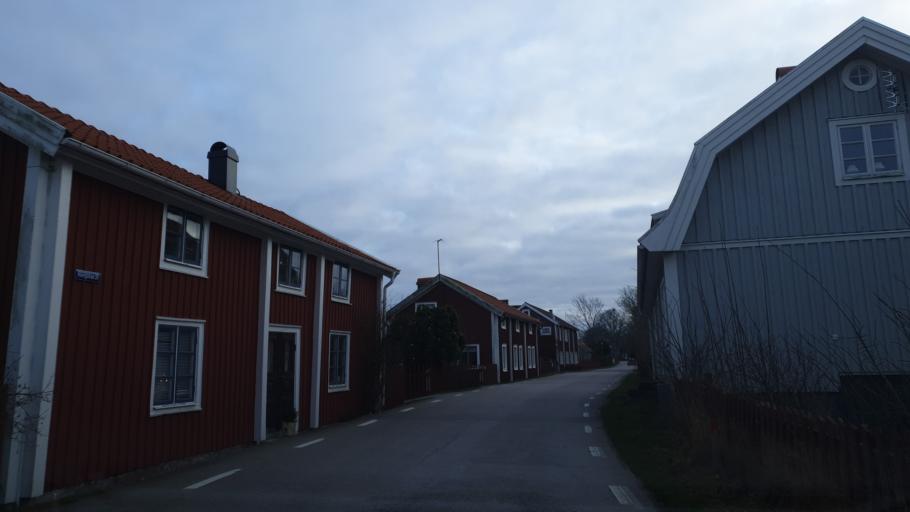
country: SE
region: Kalmar
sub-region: Torsas Kommun
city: Torsas
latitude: 56.2598
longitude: 16.0408
